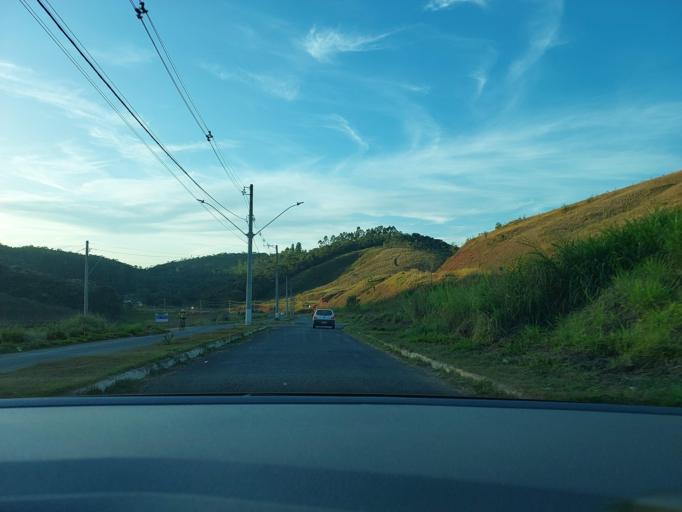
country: BR
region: Minas Gerais
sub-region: Vicosa
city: Vicosa
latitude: -20.7865
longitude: -42.8391
